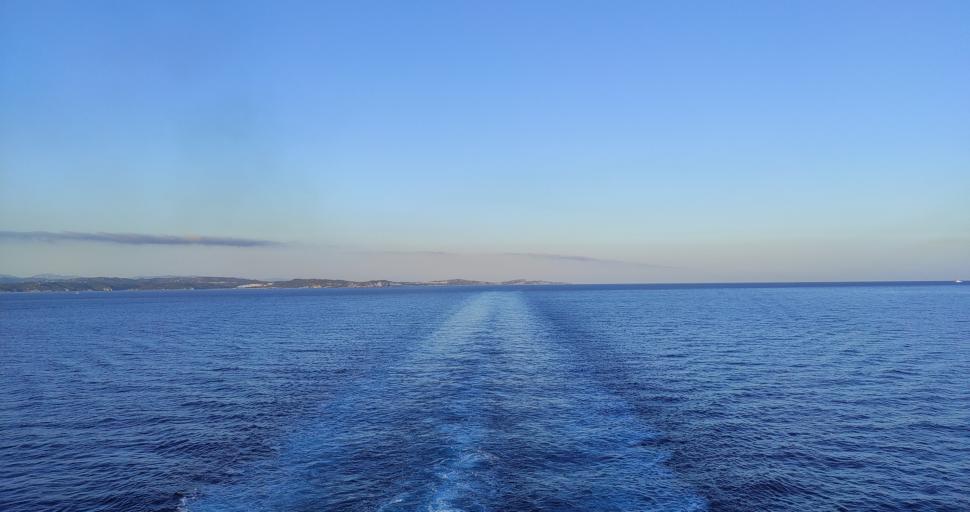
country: IT
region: Sardinia
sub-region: Provincia di Olbia-Tempio
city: Santa Teresa Gallura
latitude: 41.3075
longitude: 9.2935
